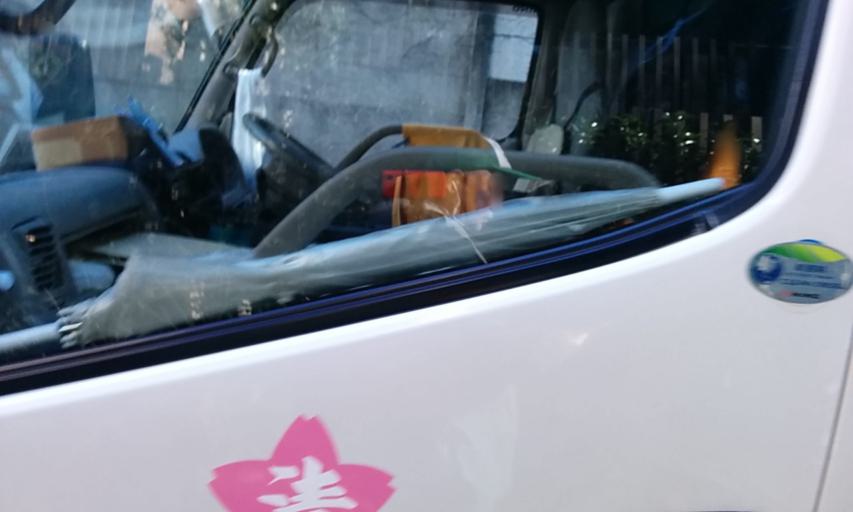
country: JP
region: Tokyo
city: Tokyo
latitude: 35.7228
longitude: 139.7417
